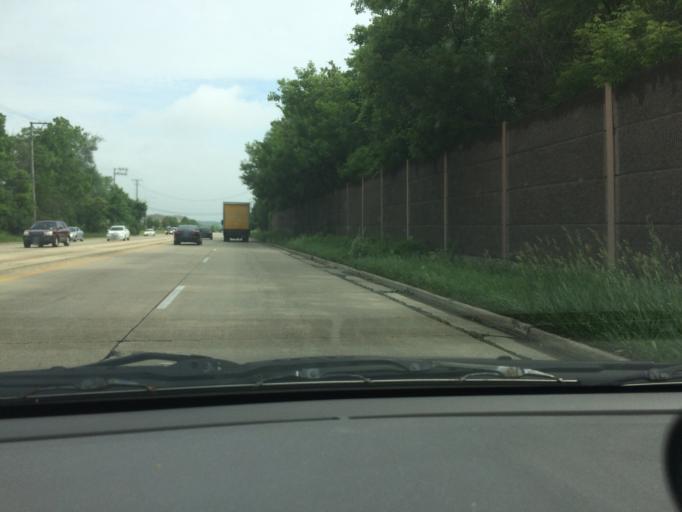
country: US
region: Illinois
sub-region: Cook County
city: Bartlett
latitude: 41.9895
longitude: -88.2073
